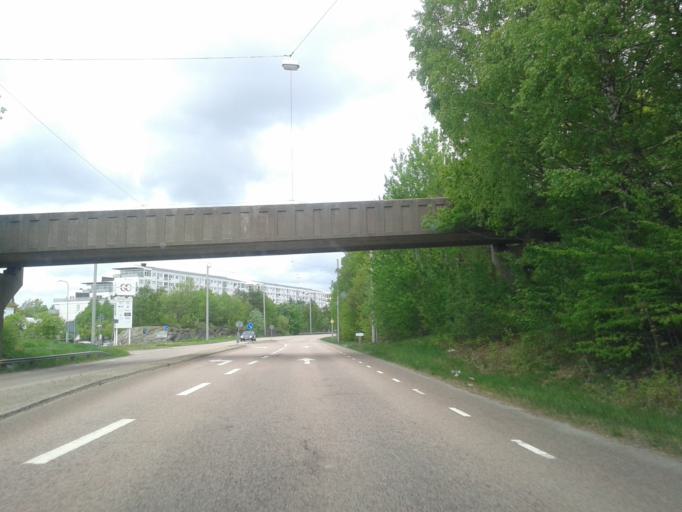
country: SE
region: Vaestra Goetaland
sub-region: Goteborg
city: Gardsten
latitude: 57.8029
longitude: 12.0343
